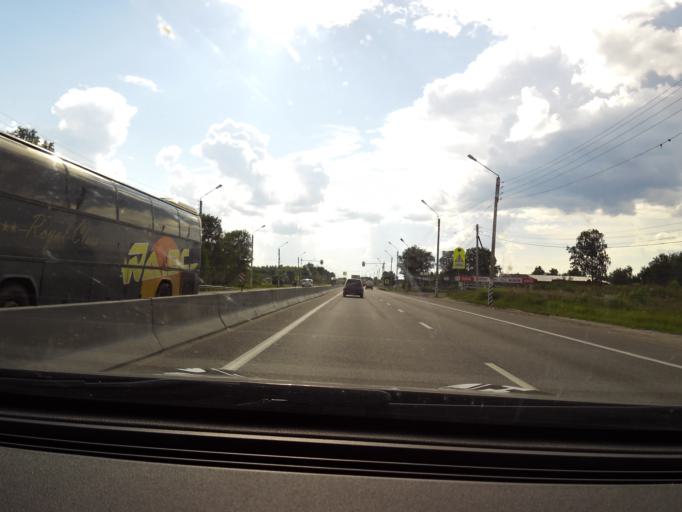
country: RU
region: Nizjnij Novgorod
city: Babino
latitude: 56.3044
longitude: 43.6212
